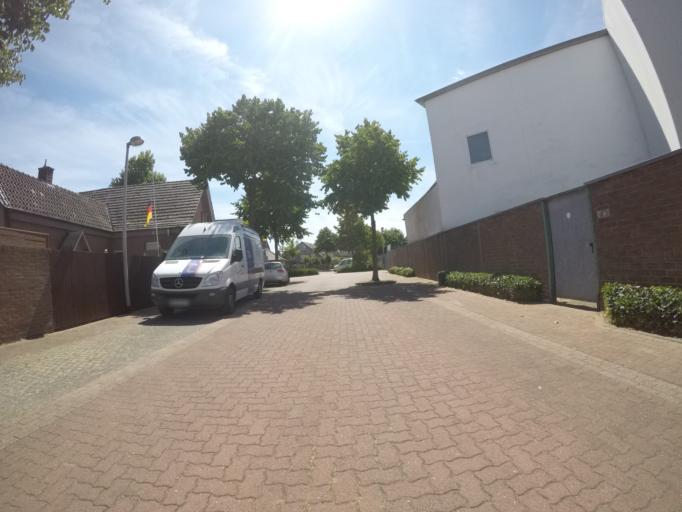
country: DE
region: North Rhine-Westphalia
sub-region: Regierungsbezirk Dusseldorf
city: Bocholt
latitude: 51.8280
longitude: 6.6118
